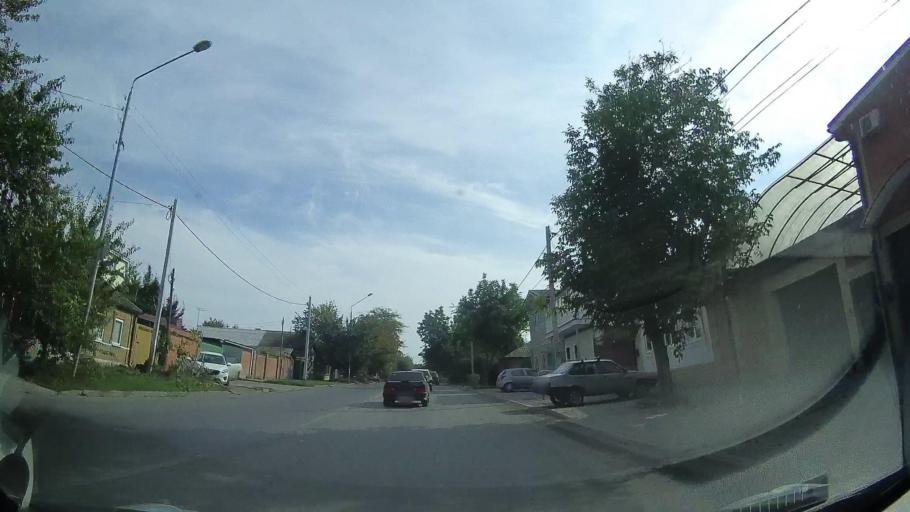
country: RU
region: Rostov
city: Severnyy
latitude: 47.2694
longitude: 39.7065
